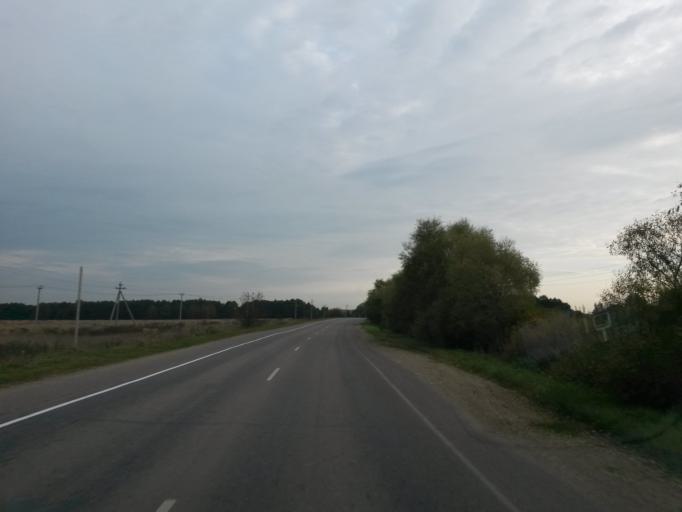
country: RU
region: Moskovskaya
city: Barybino
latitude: 55.2181
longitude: 37.7867
